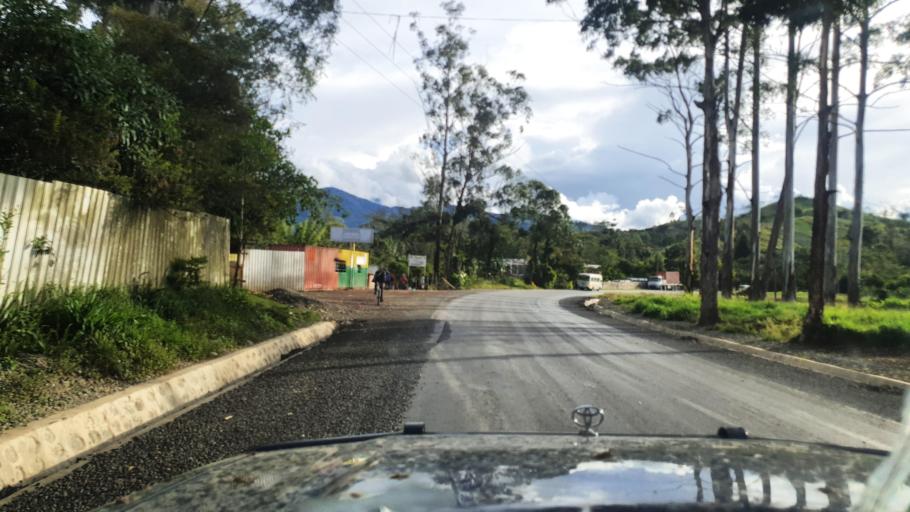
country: PG
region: Jiwaka
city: Minj
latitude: -5.8476
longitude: 144.5967
